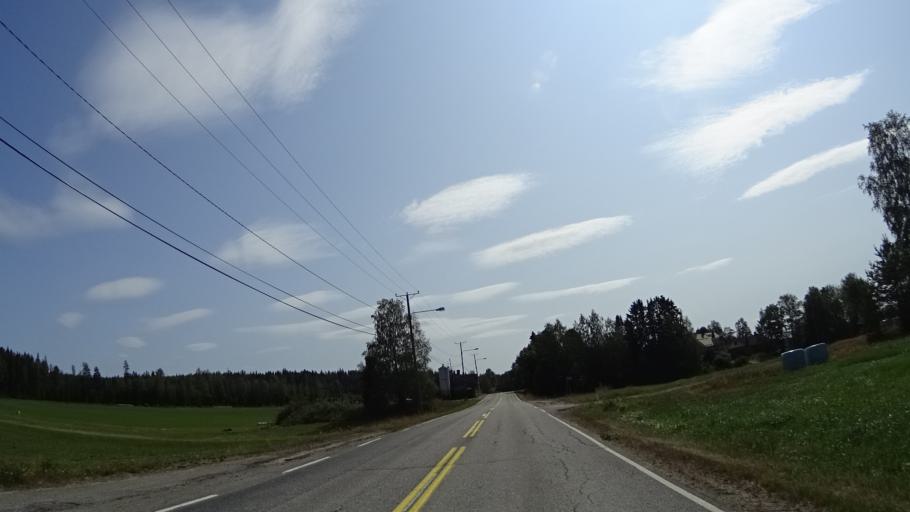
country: FI
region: Pirkanmaa
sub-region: Ylae-Pirkanmaa
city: Maenttae
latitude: 61.9111
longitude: 24.7812
